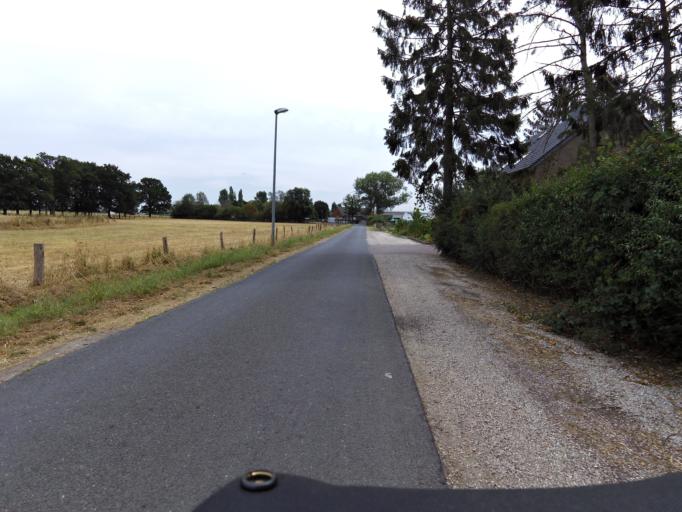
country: DE
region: North Rhine-Westphalia
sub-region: Regierungsbezirk Dusseldorf
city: Kevelaer
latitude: 51.5852
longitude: 6.2178
